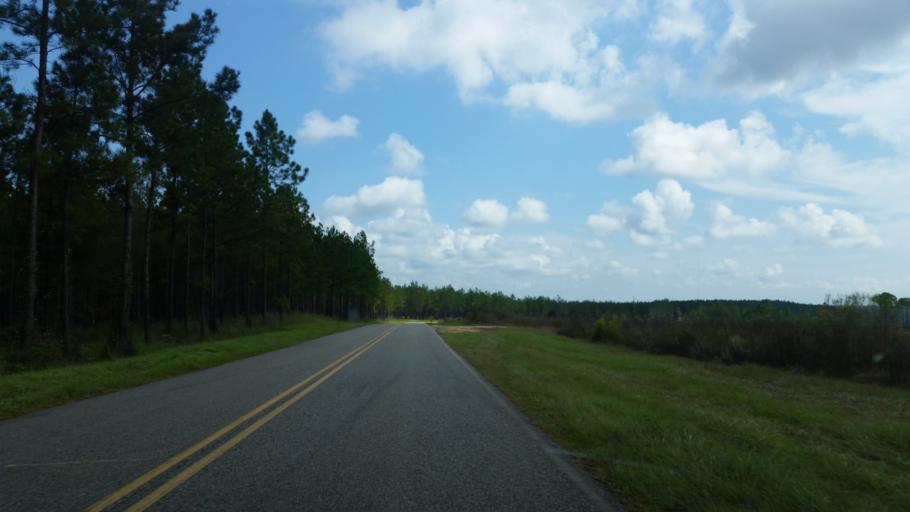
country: US
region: Florida
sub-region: Escambia County
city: Cantonment
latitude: 30.6862
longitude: -87.4622
